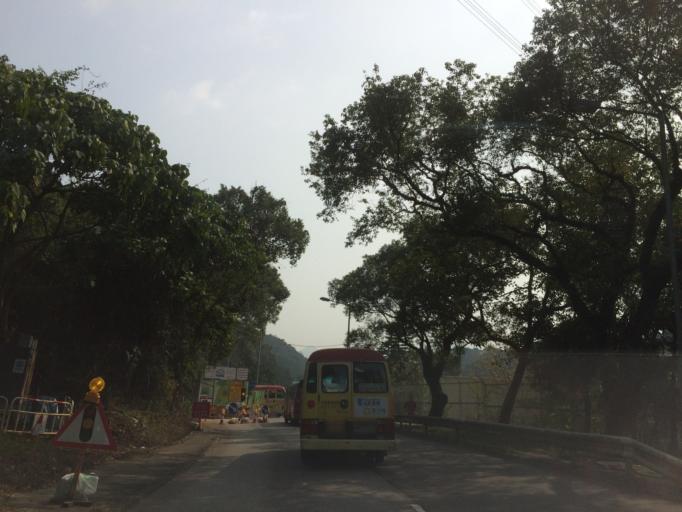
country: HK
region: Tai Po
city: Tai Po
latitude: 22.4605
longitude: 114.1487
